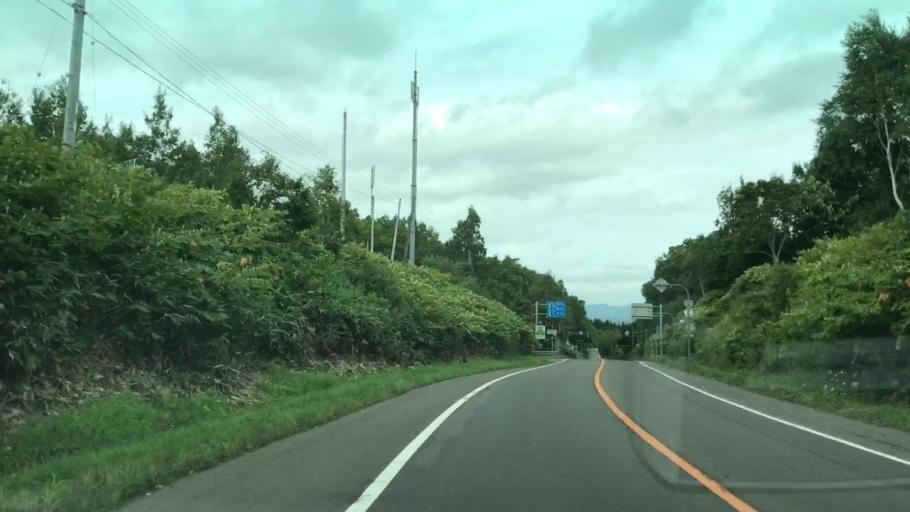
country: JP
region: Hokkaido
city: Niseko Town
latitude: 42.9232
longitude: 140.7184
